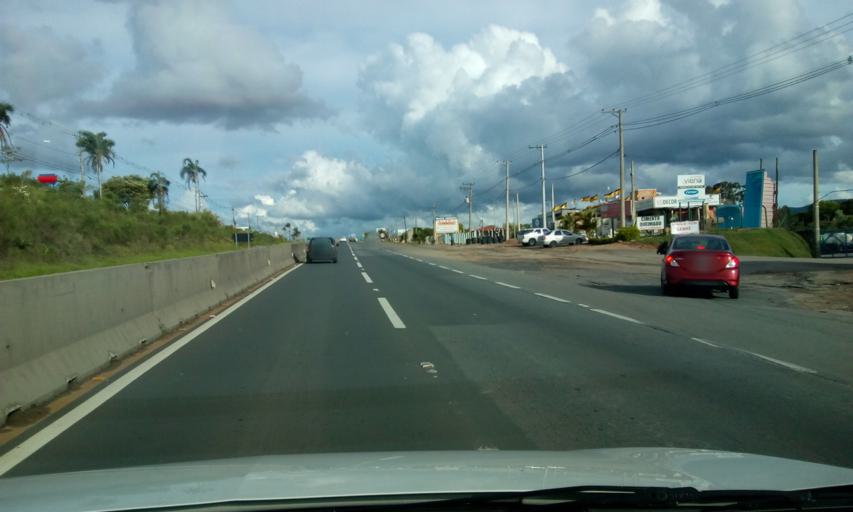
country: BR
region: Sao Paulo
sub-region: Itupeva
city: Itupeva
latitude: -23.1646
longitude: -47.0113
